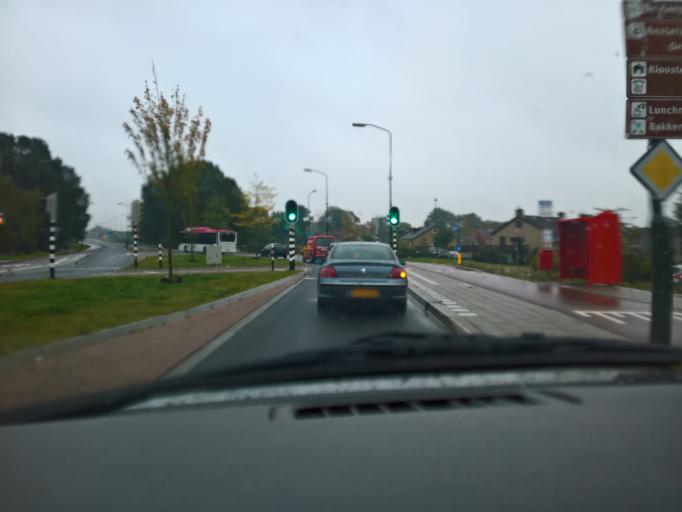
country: NL
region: Gelderland
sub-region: Gemeente Overbetuwe
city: Oosterhout
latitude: 51.8569
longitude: 5.8162
